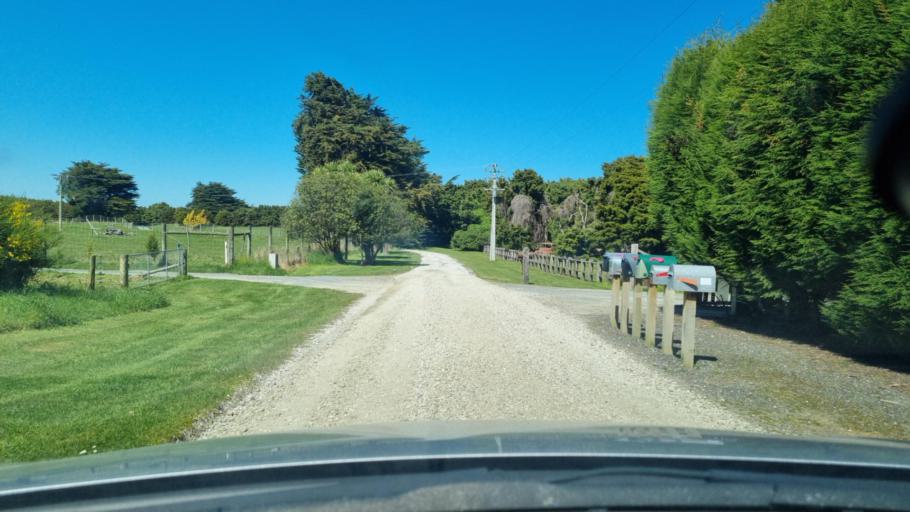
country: NZ
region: Southland
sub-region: Invercargill City
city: Invercargill
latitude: -46.4566
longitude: 168.2813
